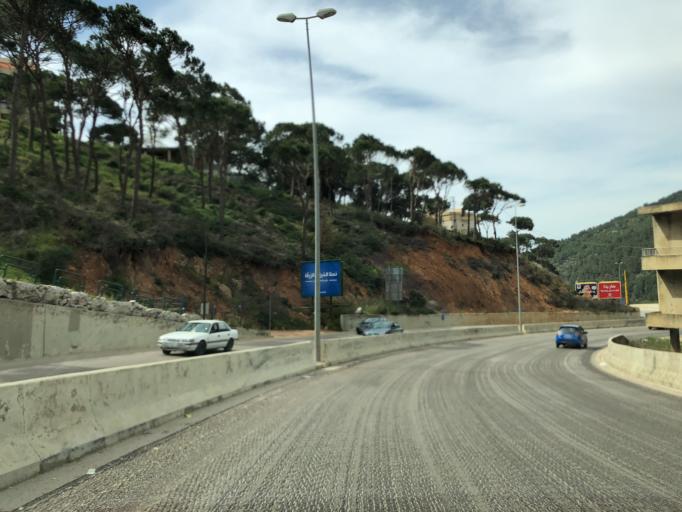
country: LB
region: Mont-Liban
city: Bhamdoun el Mhatta
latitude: 33.8899
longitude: 35.6617
